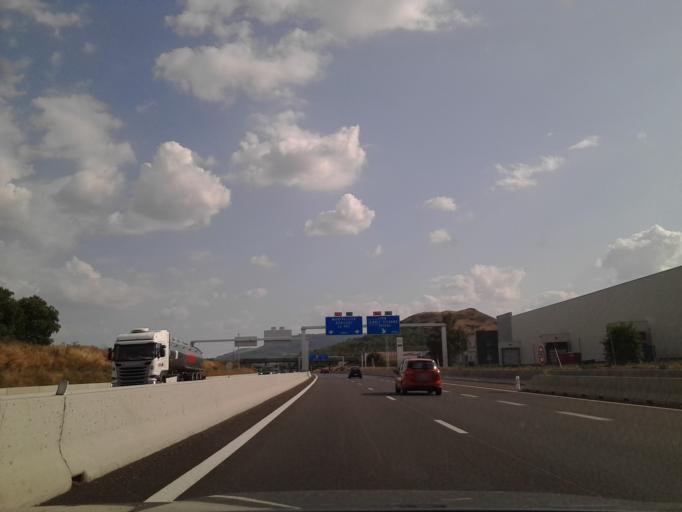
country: FR
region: Auvergne
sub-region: Departement du Puy-de-Dome
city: Aulnat
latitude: 45.7819
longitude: 3.1418
